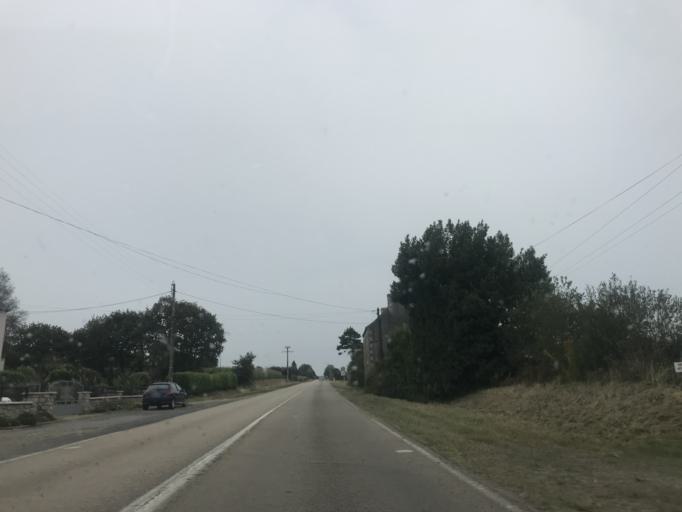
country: FR
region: Brittany
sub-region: Departement du Finistere
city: Plouneour-Menez
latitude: 48.4481
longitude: -3.8807
